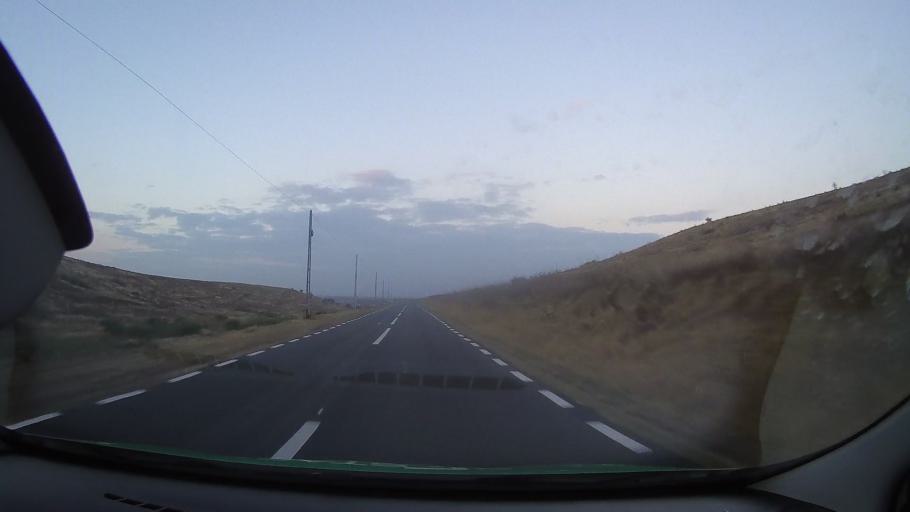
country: RO
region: Constanta
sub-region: Comuna Oltina
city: Oltina
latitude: 44.1432
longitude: 27.6660
